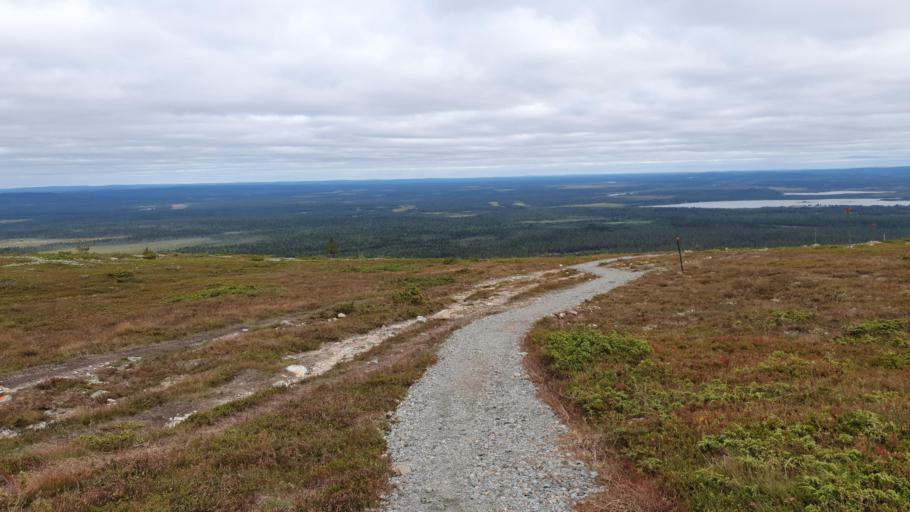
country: FI
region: Lapland
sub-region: Tunturi-Lappi
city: Kolari
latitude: 67.5664
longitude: 24.2490
